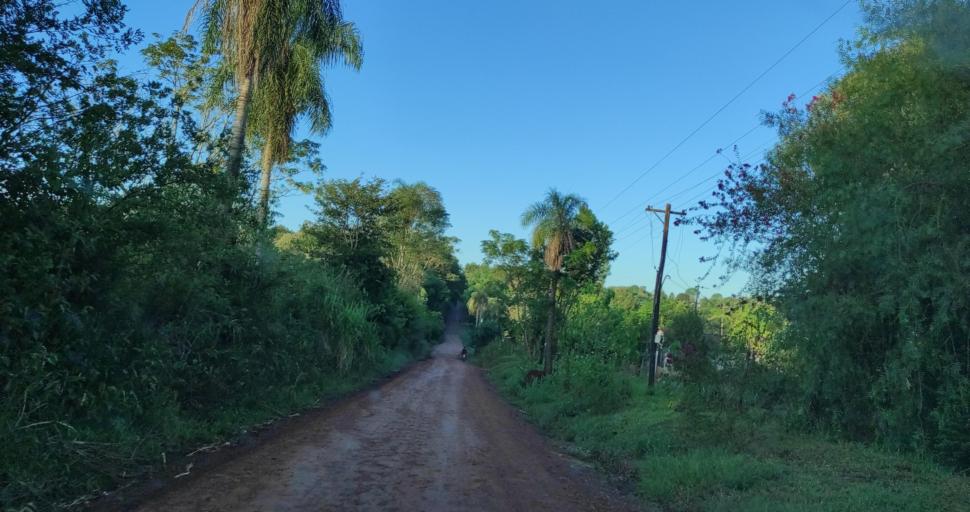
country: AR
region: Misiones
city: Gobernador Roca
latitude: -27.2201
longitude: -55.4266
